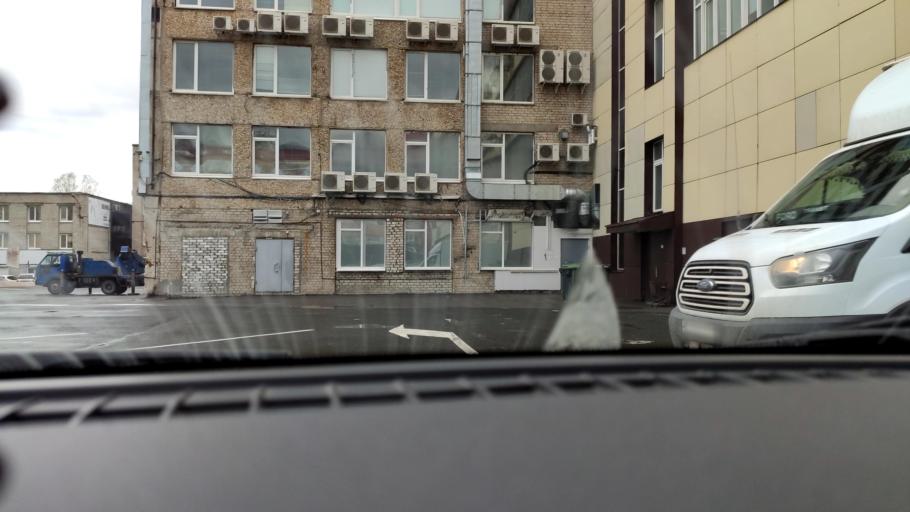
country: RU
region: Perm
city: Perm
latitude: 57.9889
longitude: 56.2057
